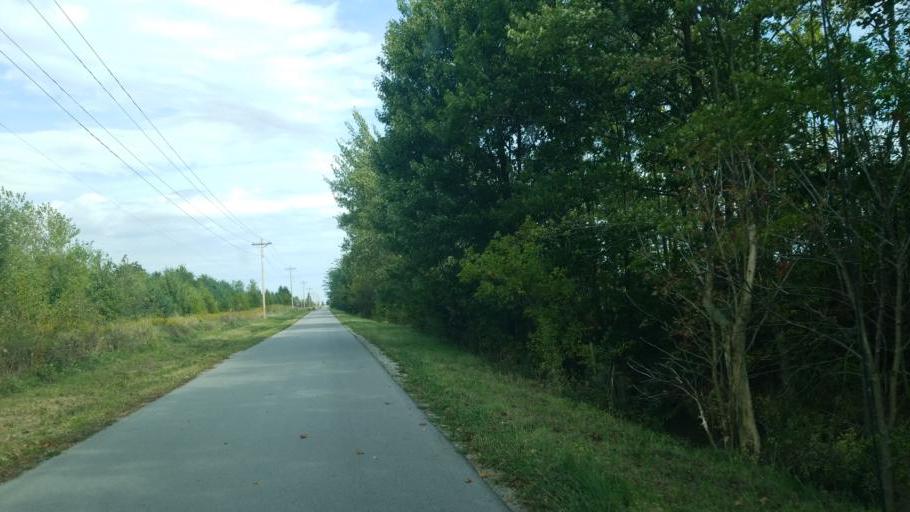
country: US
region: Ohio
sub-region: Hardin County
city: Forest
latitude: 40.8546
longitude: -83.5281
